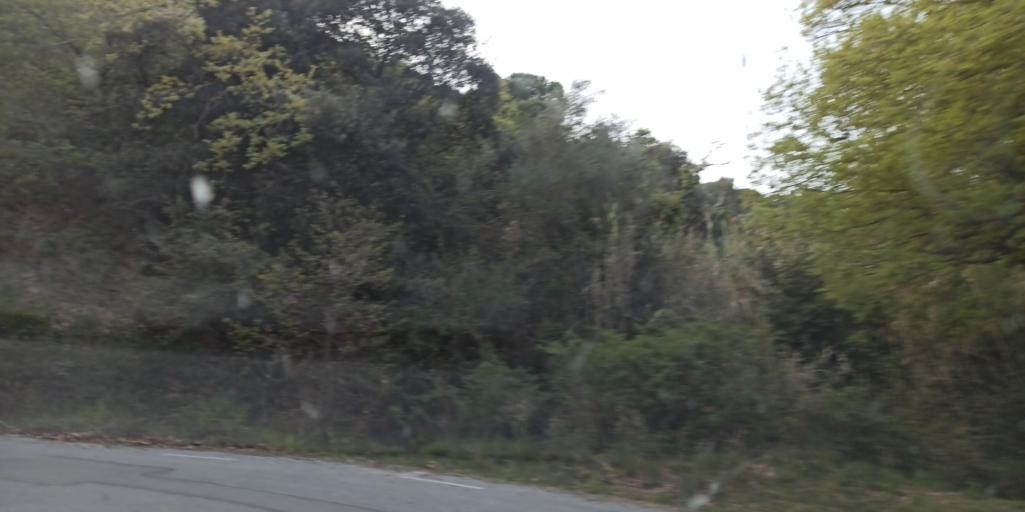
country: ES
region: Catalonia
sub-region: Provincia de Barcelona
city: Sant Just Desvern
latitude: 41.4060
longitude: 2.0877
